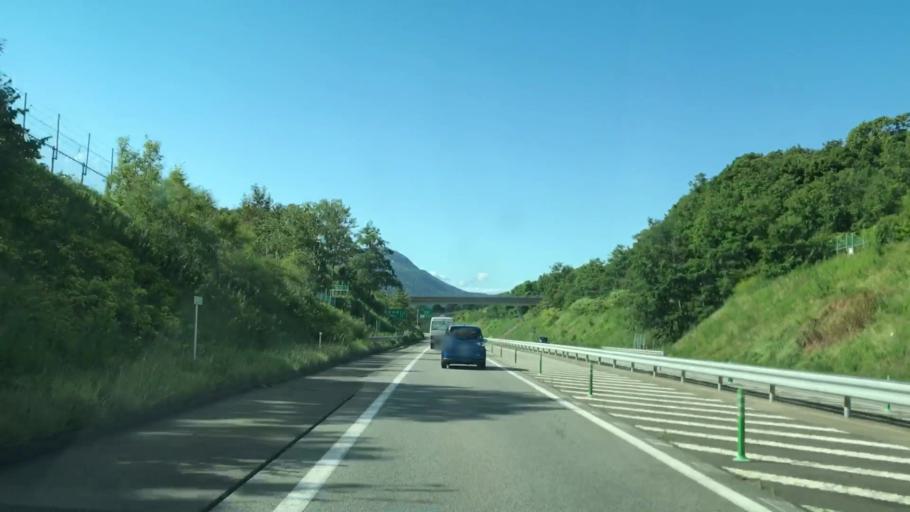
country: JP
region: Hokkaido
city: Date
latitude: 42.4768
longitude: 140.9016
